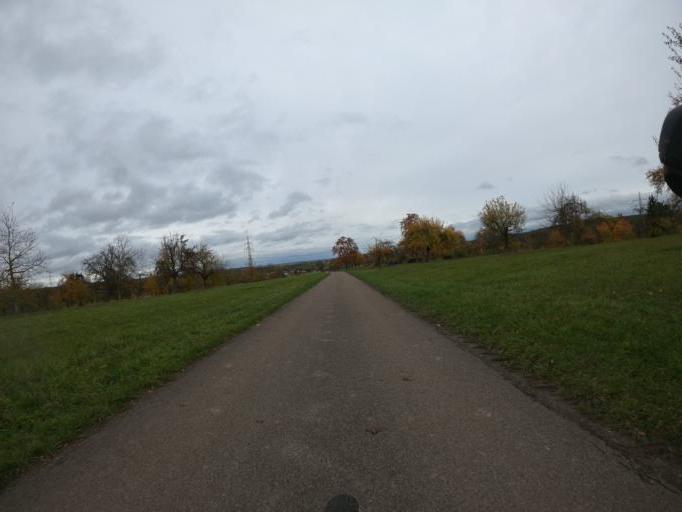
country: DE
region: Baden-Wuerttemberg
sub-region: Regierungsbezirk Stuttgart
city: Hildrizhausen
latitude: 48.6238
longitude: 8.9527
